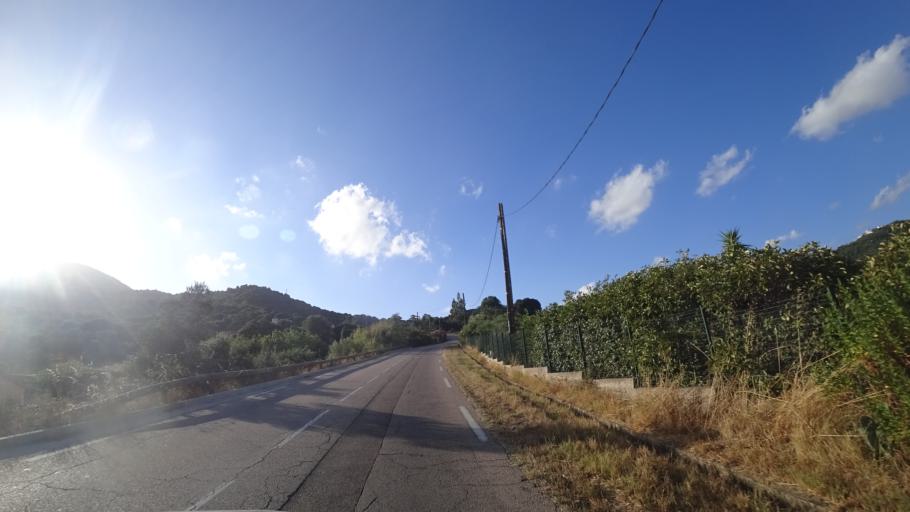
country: FR
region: Corsica
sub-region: Departement de la Corse-du-Sud
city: Alata
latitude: 41.9561
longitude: 8.7285
